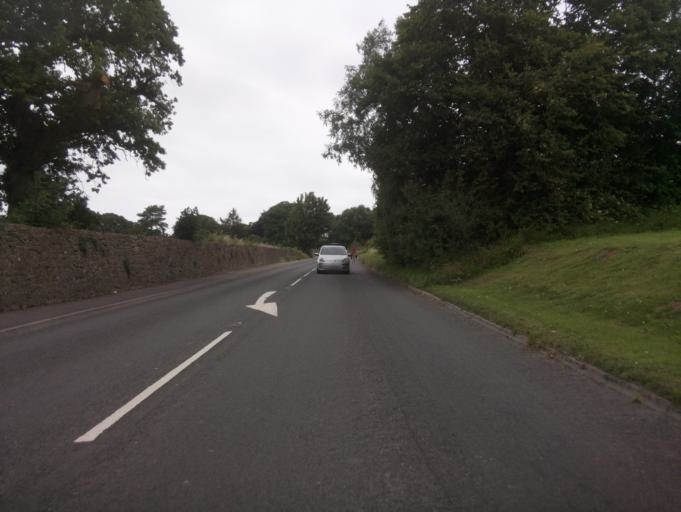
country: GB
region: England
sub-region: North Somerset
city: Congresbury
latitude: 51.3783
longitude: -2.8103
